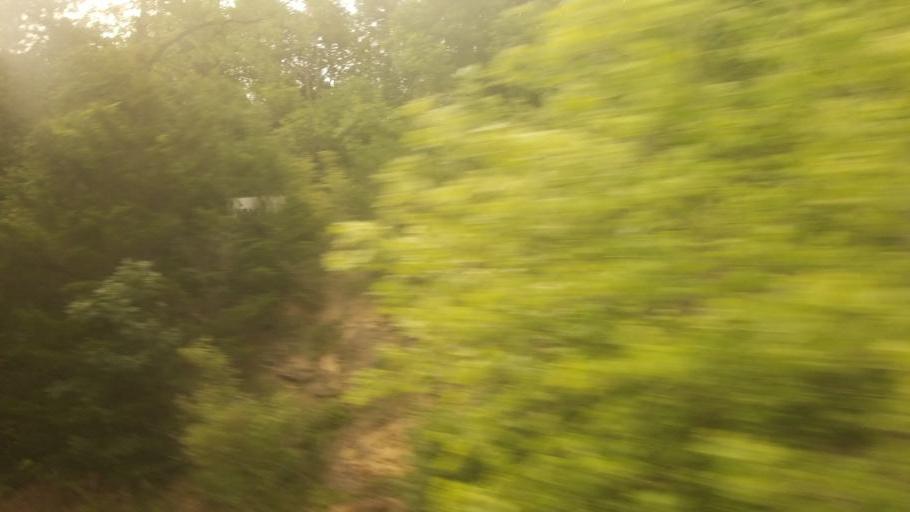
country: US
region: Kansas
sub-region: Shawnee County
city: Topeka
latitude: 39.0554
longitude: -95.4798
